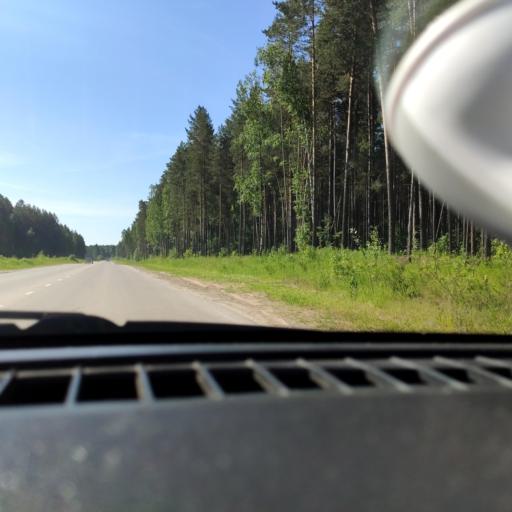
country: RU
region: Perm
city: Overyata
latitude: 58.0036
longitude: 55.8779
